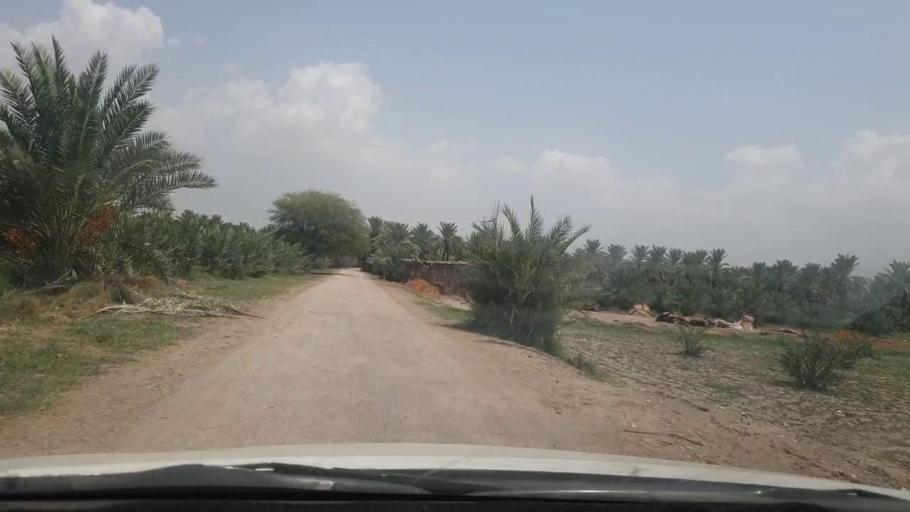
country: PK
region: Sindh
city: Khairpur
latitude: 27.5505
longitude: 68.8322
